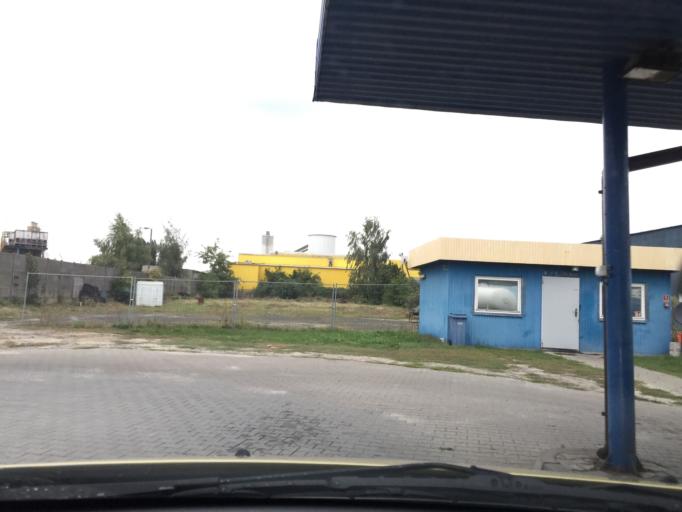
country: PL
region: Greater Poland Voivodeship
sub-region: Kalisz
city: Kalisz
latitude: 51.7426
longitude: 18.0627
